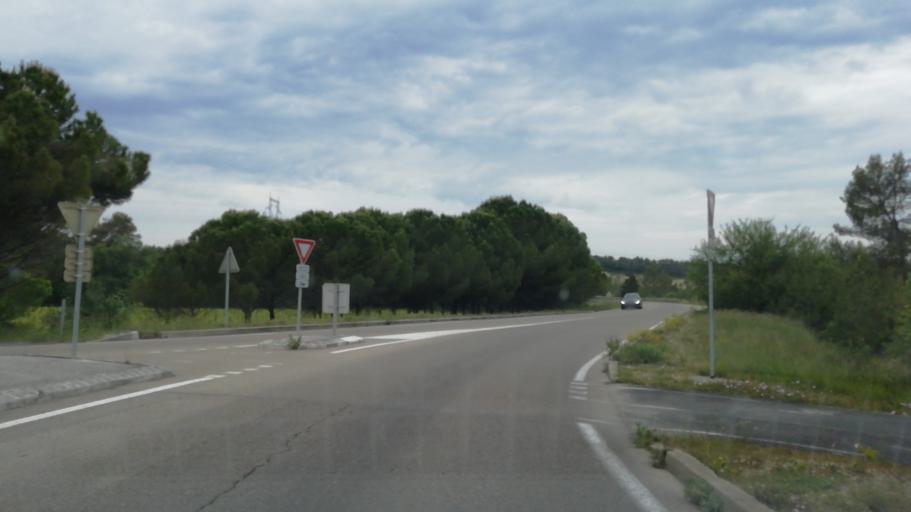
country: FR
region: Languedoc-Roussillon
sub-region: Departement de l'Herault
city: Saint-Gely-du-Fesc
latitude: 43.7070
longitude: 3.8238
